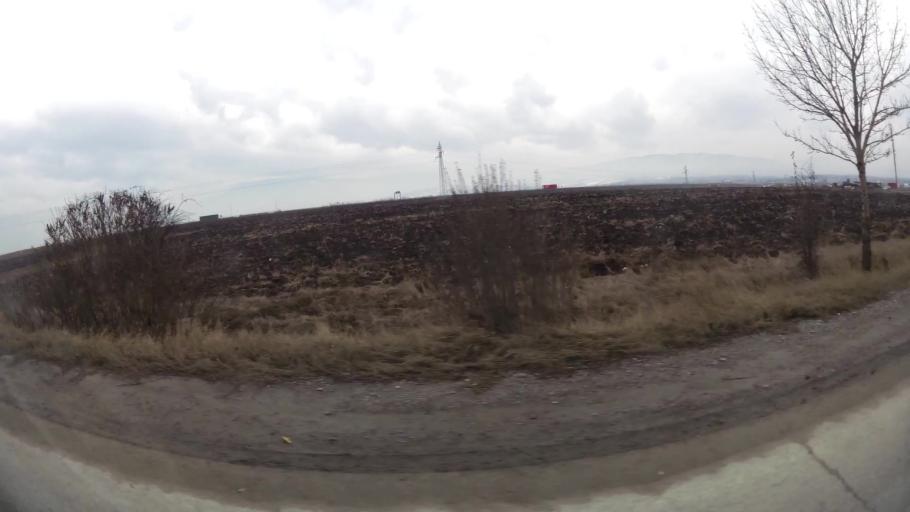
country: BG
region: Sofiya
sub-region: Obshtina Bozhurishte
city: Bozhurishte
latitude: 42.7139
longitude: 23.2238
